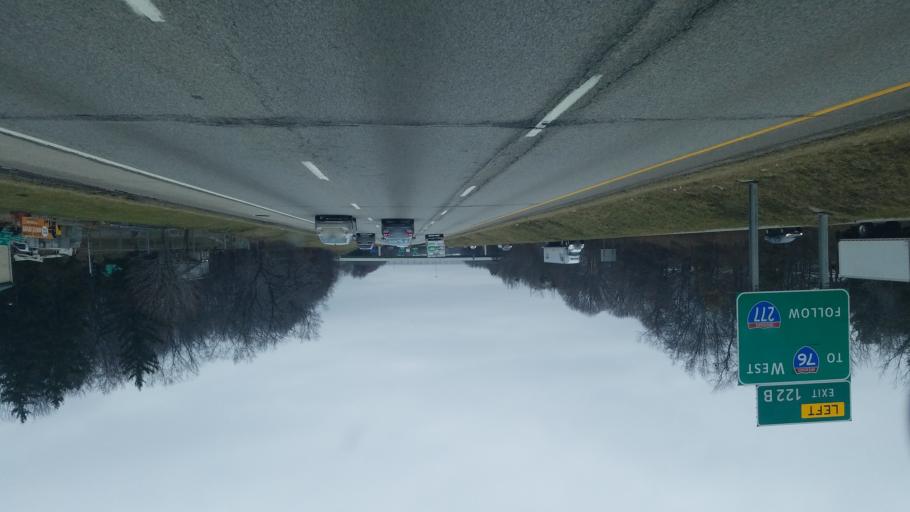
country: US
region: Ohio
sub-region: Summit County
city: Portage Lakes
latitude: 41.0149
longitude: -81.4956
